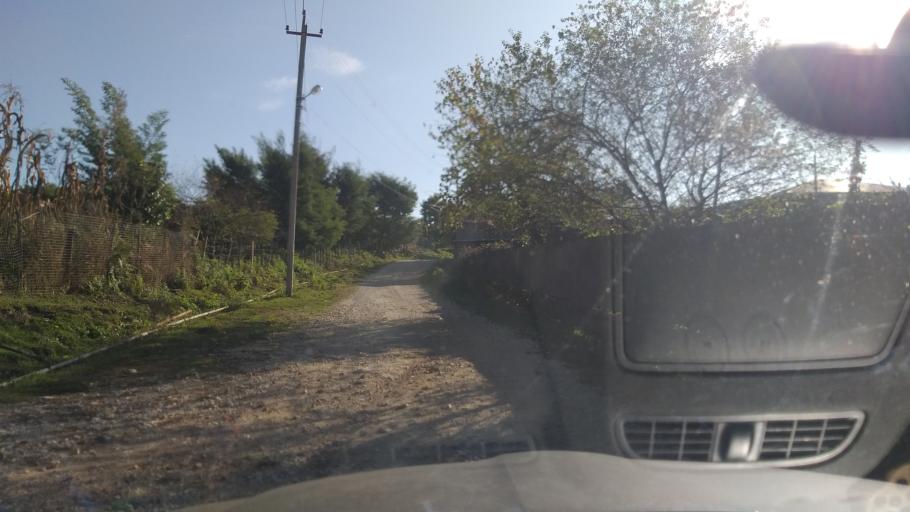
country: GE
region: Abkhazia
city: Stantsiya Novyy Afon
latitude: 43.0609
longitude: 40.8922
